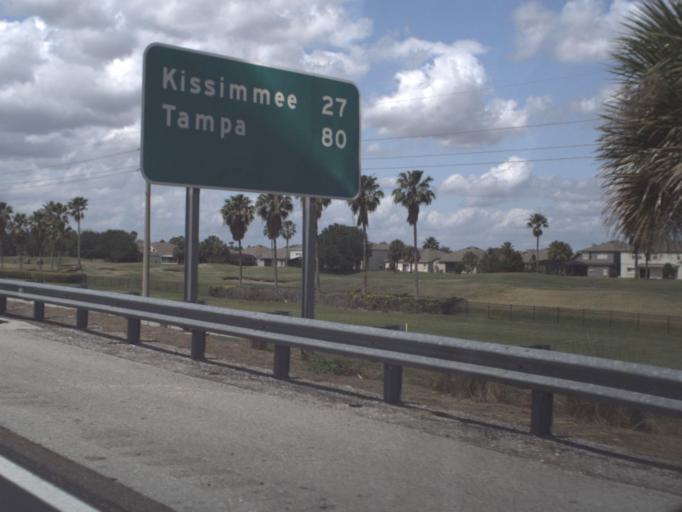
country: US
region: Florida
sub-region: Orange County
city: Oakland
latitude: 28.5138
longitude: -81.6025
